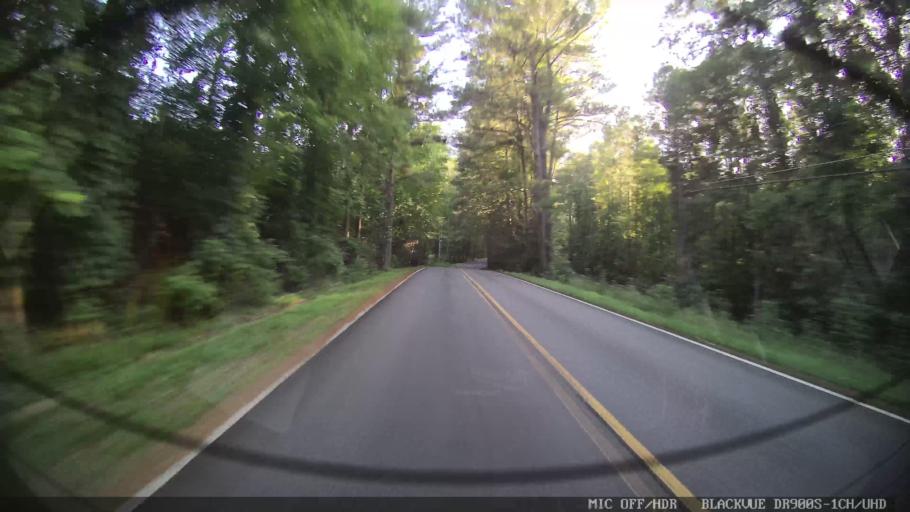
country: US
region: Georgia
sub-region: Bartow County
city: Emerson
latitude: 34.1899
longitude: -84.7040
